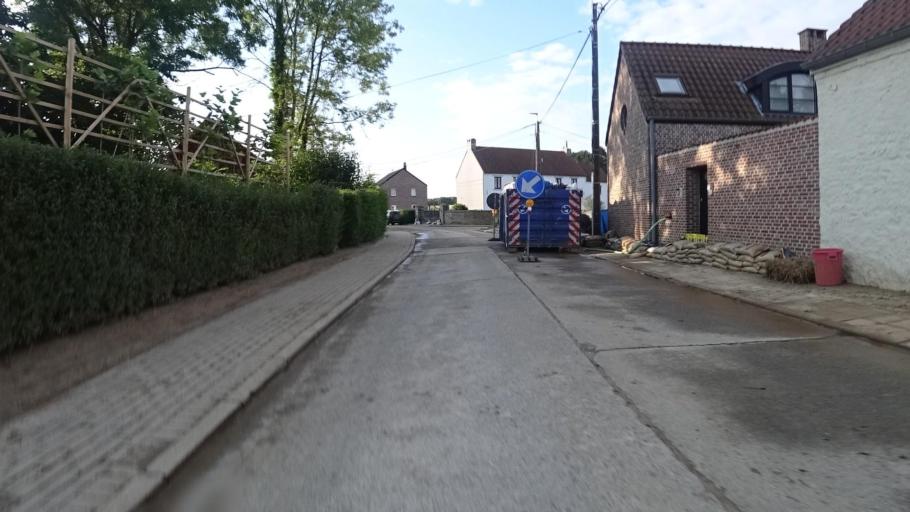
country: BE
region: Wallonia
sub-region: Province du Brabant Wallon
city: Walhain-Saint-Paul
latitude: 50.6459
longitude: 4.6878
